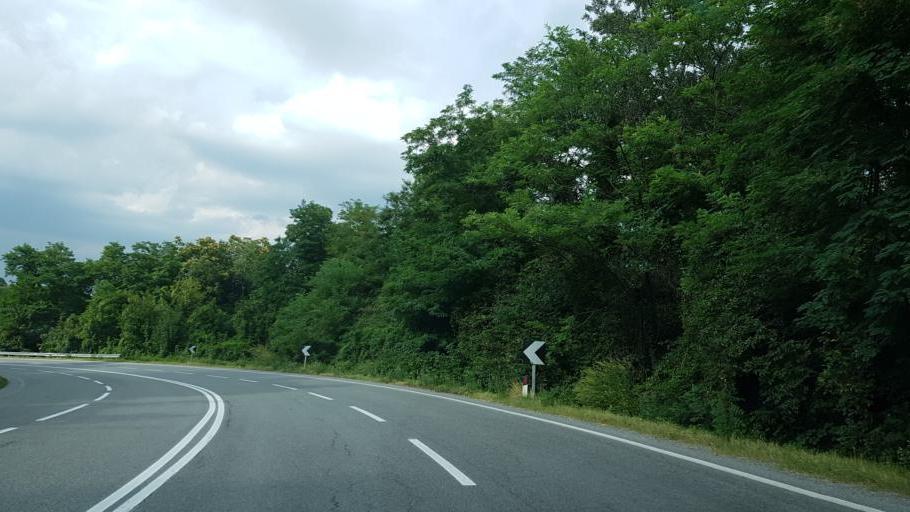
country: IT
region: Piedmont
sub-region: Provincia di Cuneo
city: Borgo San Dalmazzo
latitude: 44.3438
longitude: 7.4767
